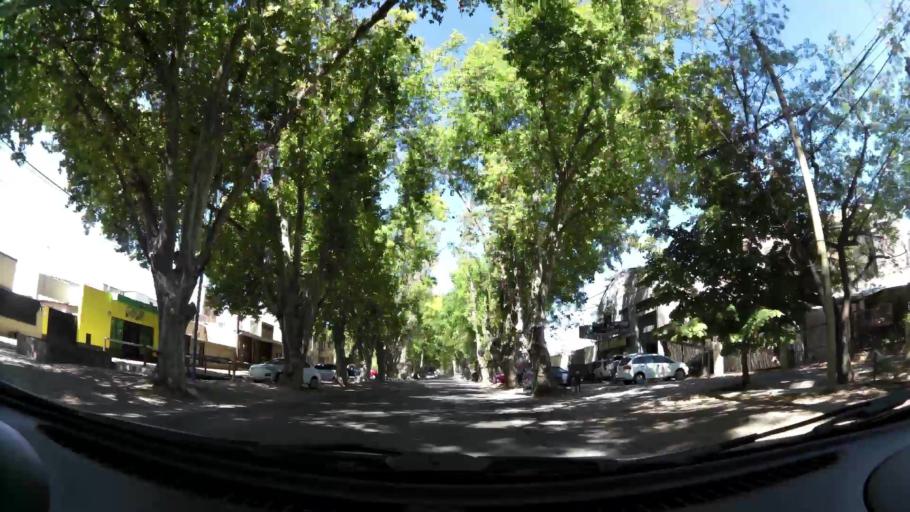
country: AR
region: Mendoza
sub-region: Departamento de Godoy Cruz
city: Godoy Cruz
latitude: -32.9499
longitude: -68.8446
